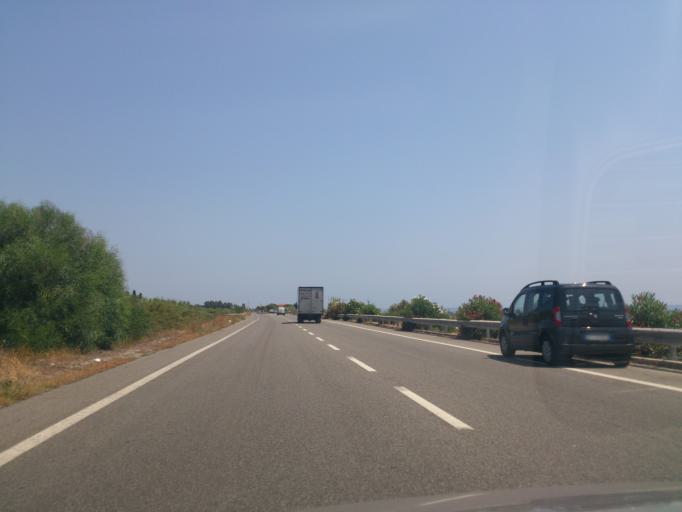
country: IT
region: Calabria
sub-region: Provincia di Reggio Calabria
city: Monasterace Marina
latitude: 38.4108
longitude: 16.5538
